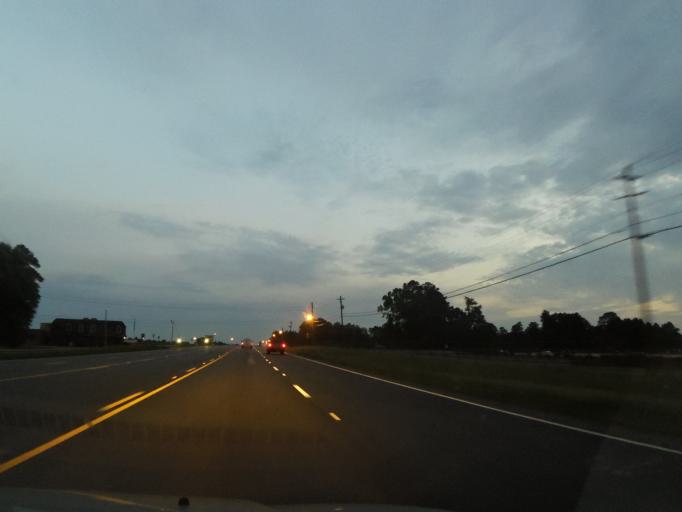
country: US
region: Georgia
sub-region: McDuffie County
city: Thomson
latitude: 33.5202
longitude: -82.5039
